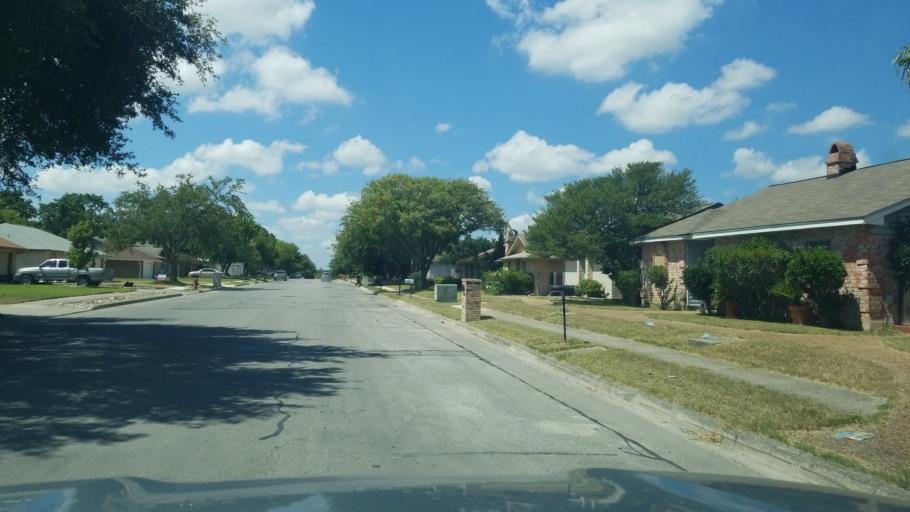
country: US
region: Texas
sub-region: Bexar County
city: Universal City
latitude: 29.5408
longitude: -98.3118
